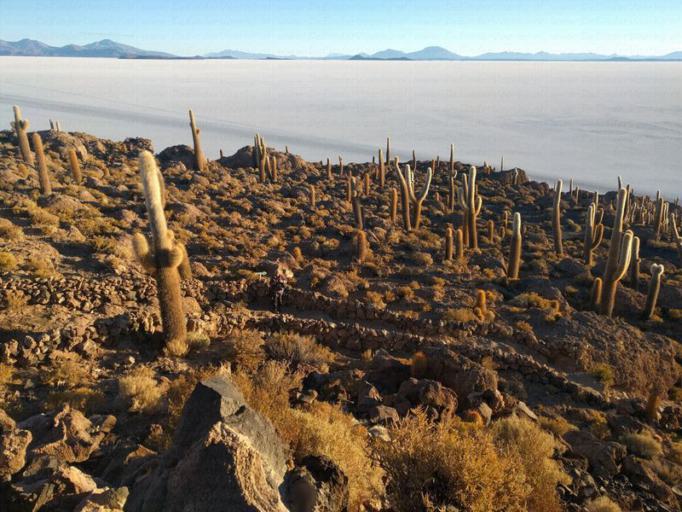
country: BO
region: Potosi
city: Colchani
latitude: -20.2428
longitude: -67.6259
